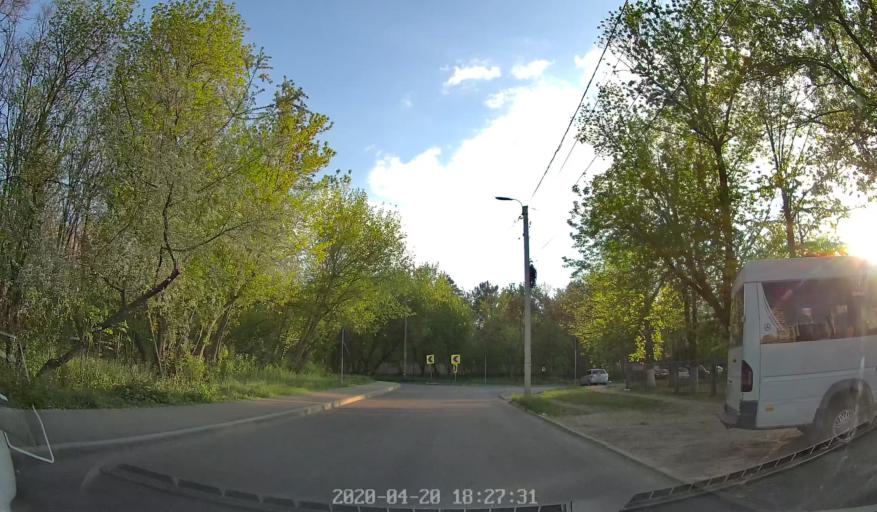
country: MD
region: Chisinau
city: Chisinau
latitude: 46.9899
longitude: 28.8357
